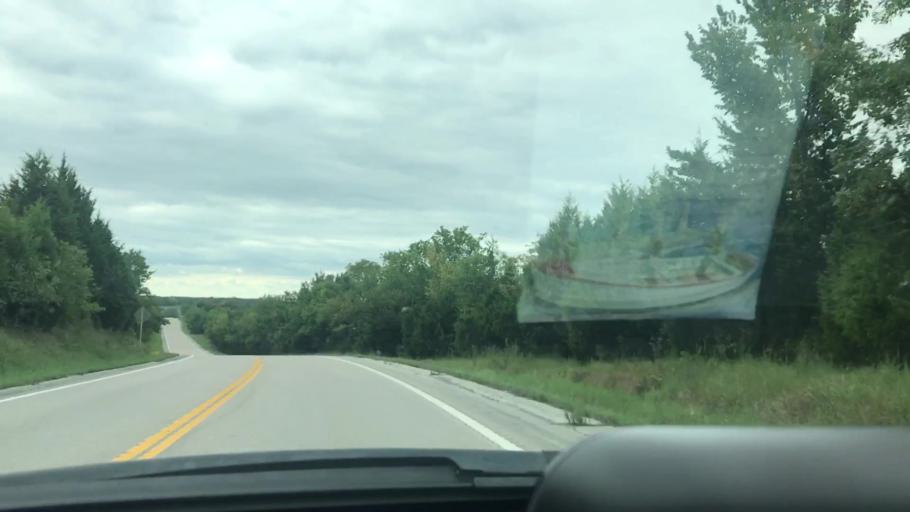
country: US
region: Missouri
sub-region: Benton County
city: Warsaw
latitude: 38.1700
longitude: -93.3109
